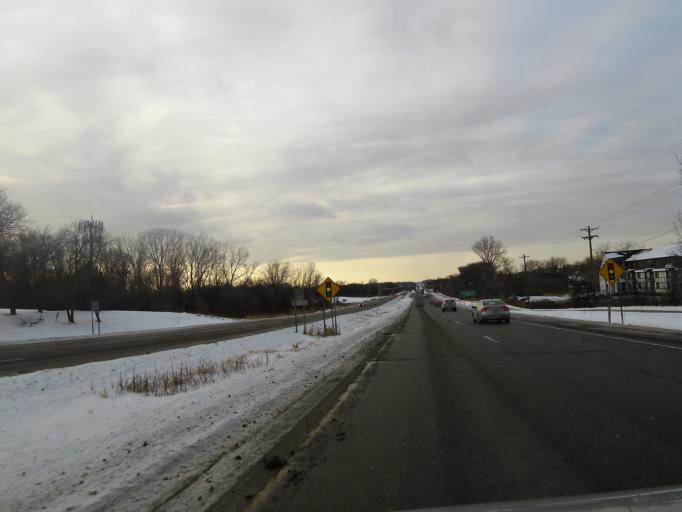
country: US
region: Minnesota
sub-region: Dakota County
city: West Saint Paul
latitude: 44.8835
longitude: -93.1007
